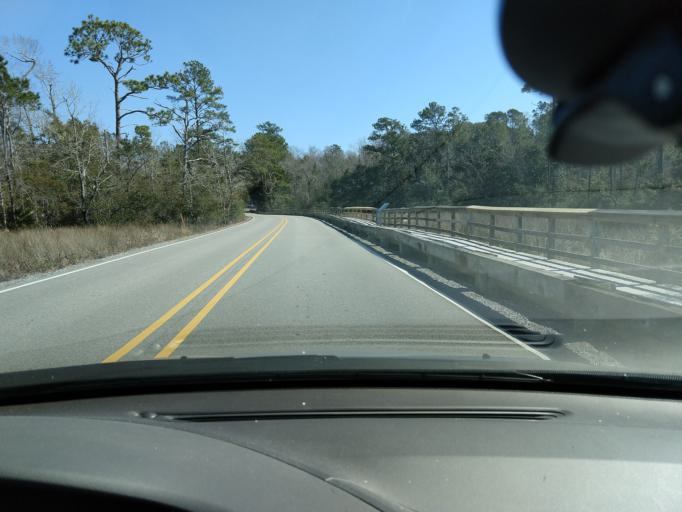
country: US
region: Mississippi
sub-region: Jackson County
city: Gulf Park Estates
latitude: 30.3978
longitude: -88.7913
